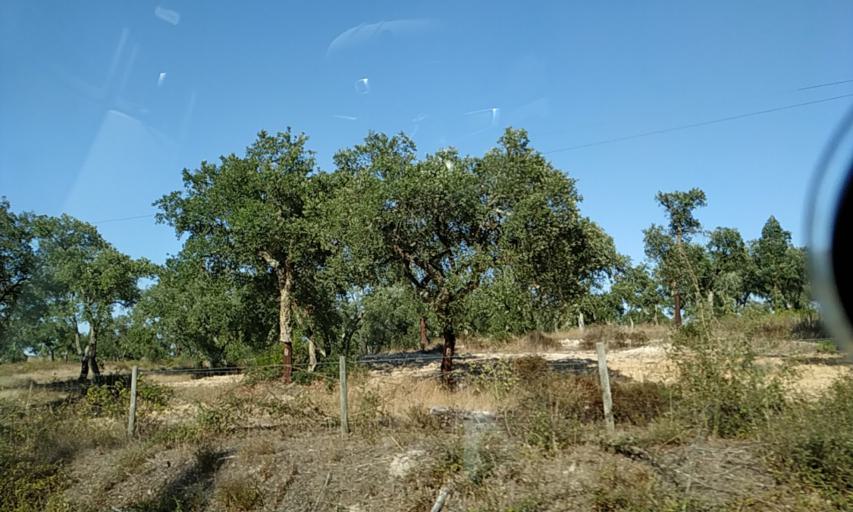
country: PT
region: Santarem
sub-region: Coruche
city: Coruche
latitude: 39.0503
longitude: -8.5648
